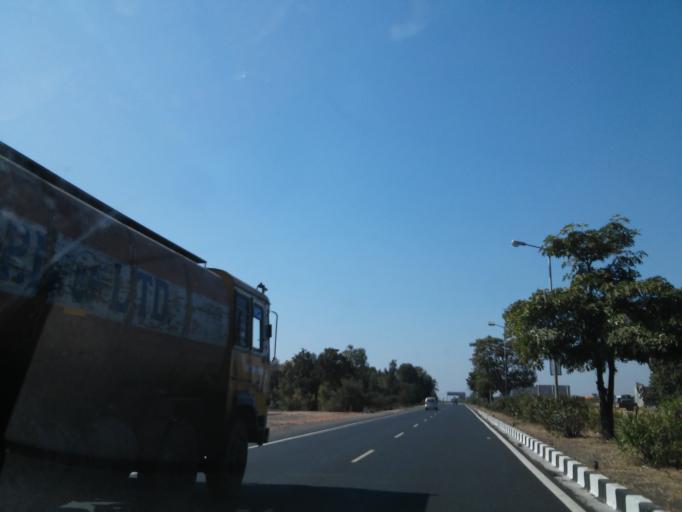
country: IN
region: Gujarat
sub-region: Sabar Kantha
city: Modasa
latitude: 23.6150
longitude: 73.2503
